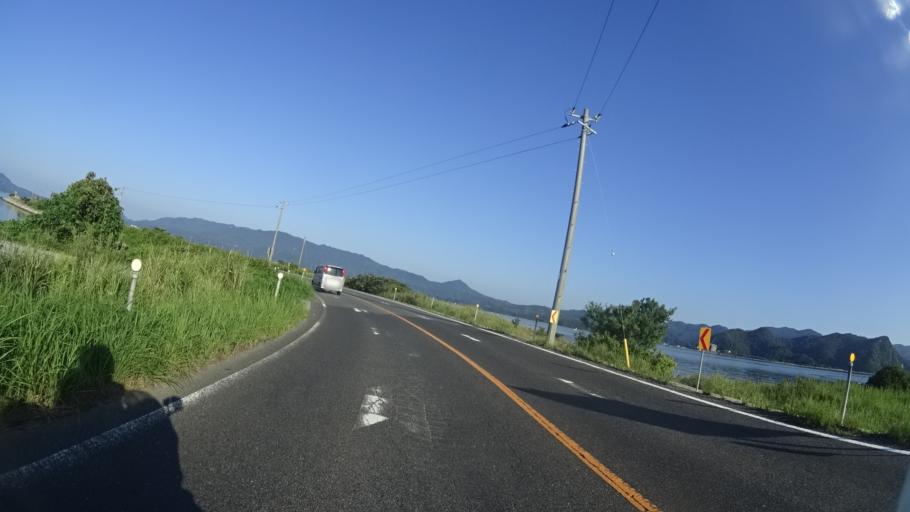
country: JP
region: Shimane
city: Sakaiminato
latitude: 35.5176
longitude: 133.1879
